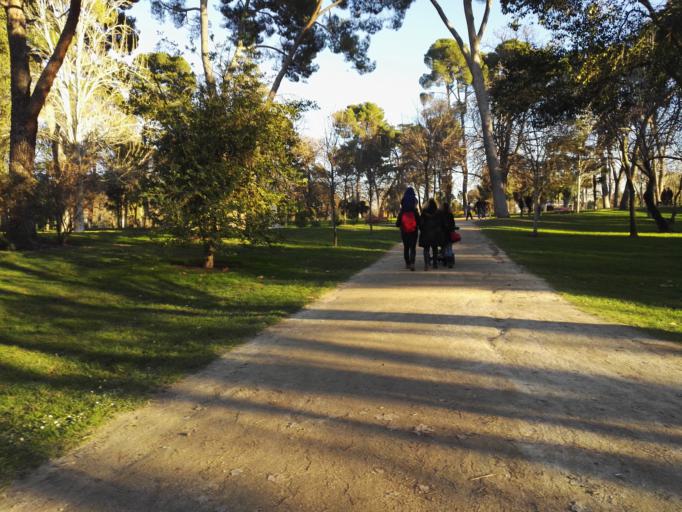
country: ES
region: Madrid
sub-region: Provincia de Madrid
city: Retiro
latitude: 40.4125
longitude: -3.6813
